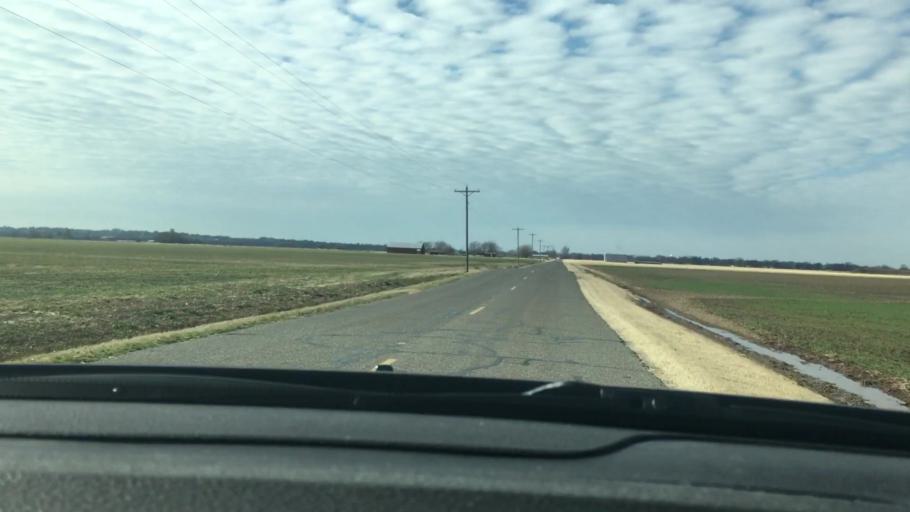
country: US
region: Oklahoma
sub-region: Garvin County
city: Pauls Valley
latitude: 34.7387
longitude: -97.1791
